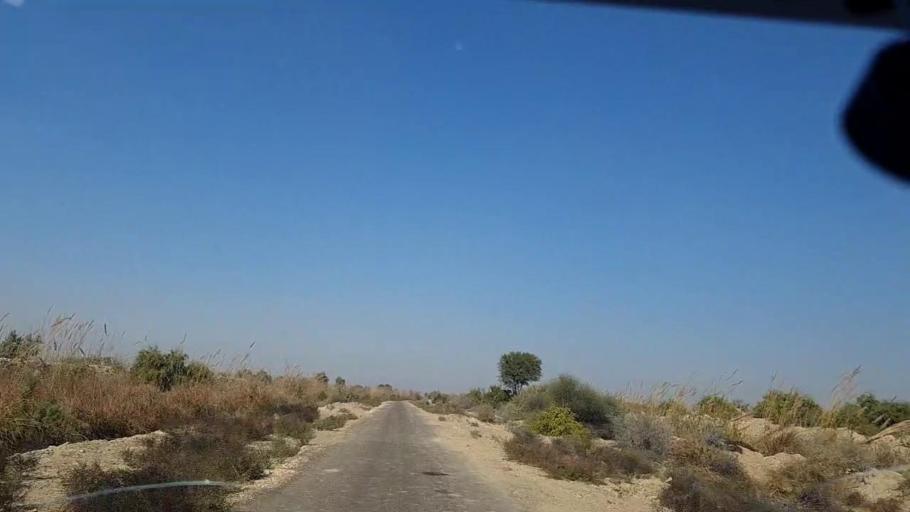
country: PK
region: Sindh
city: Khanpur
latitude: 27.5895
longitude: 69.3757
